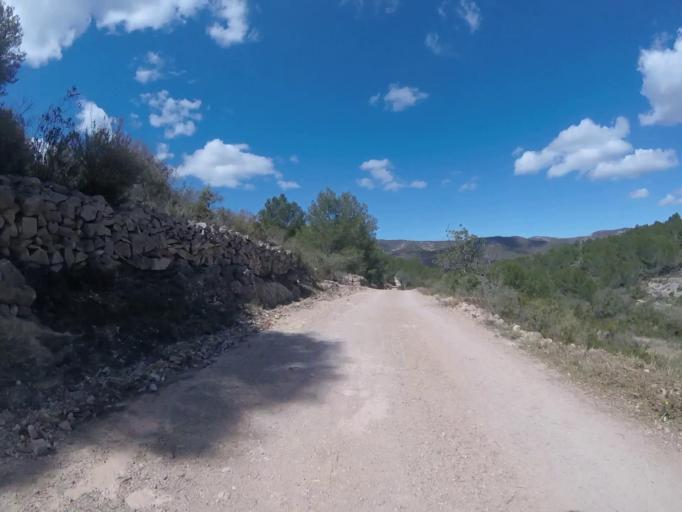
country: ES
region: Valencia
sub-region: Provincia de Castello
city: Santa Magdalena de Pulpis
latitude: 40.3232
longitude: 0.3479
